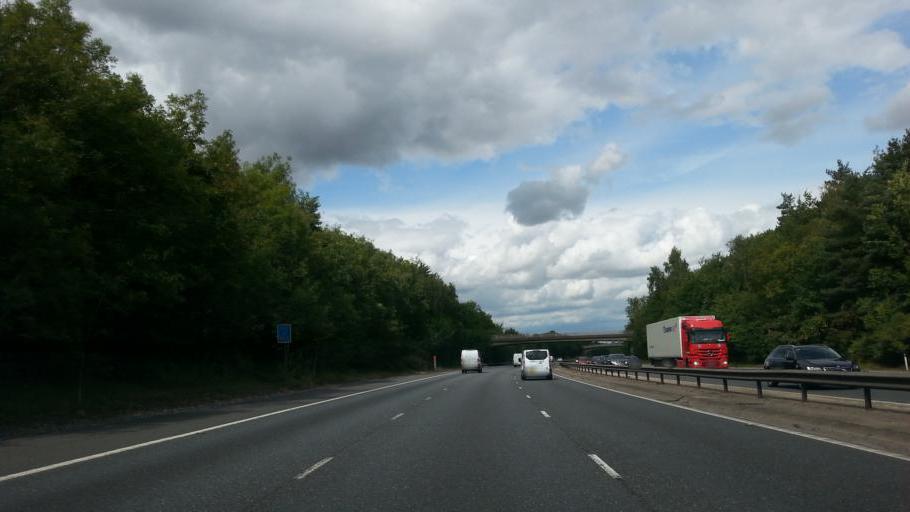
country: GB
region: England
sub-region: Essex
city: Little Hallingbury
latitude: 51.8482
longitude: 0.1851
